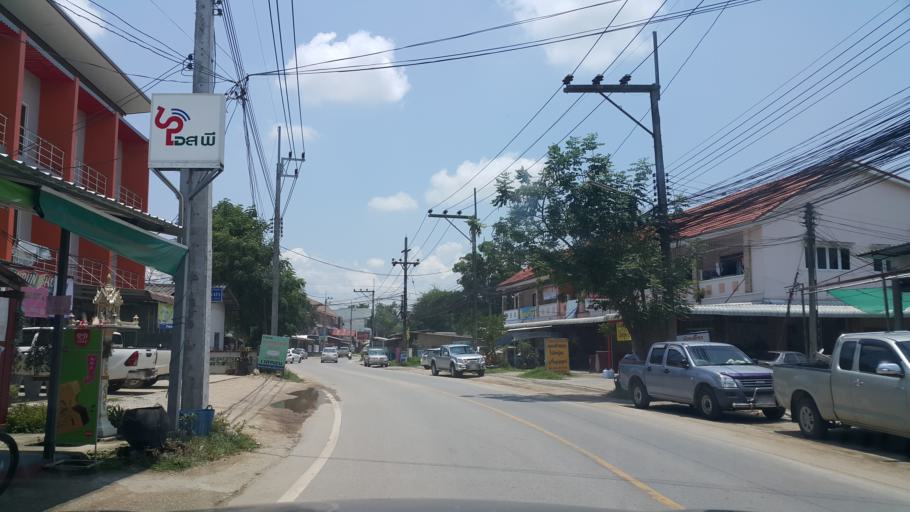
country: TH
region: Chiang Rai
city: Chiang Rai
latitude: 19.9257
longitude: 99.8163
